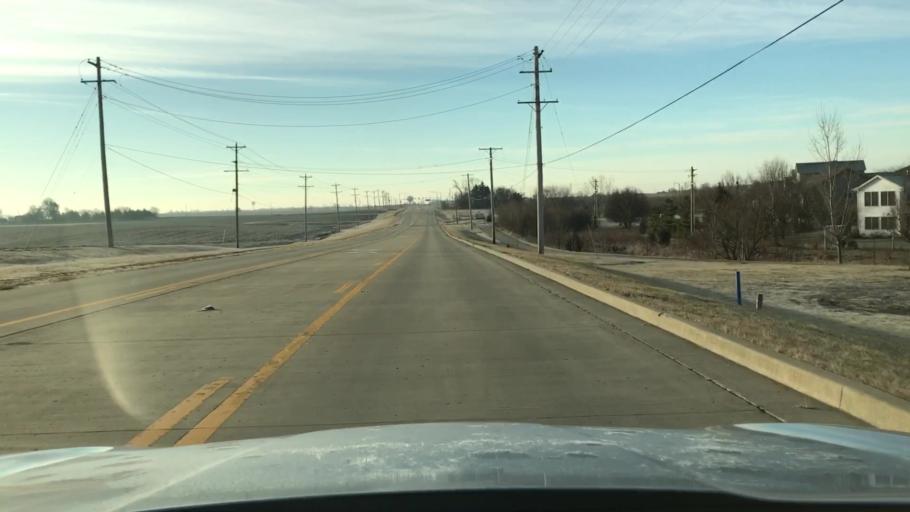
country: US
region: Illinois
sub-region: McLean County
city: Normal
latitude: 40.5536
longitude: -88.9445
